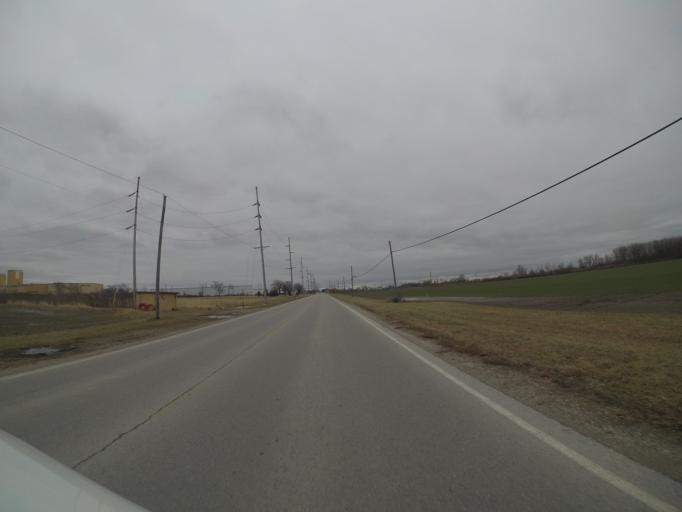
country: US
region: Ohio
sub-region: Wood County
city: Walbridge
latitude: 41.5985
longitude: -83.5128
